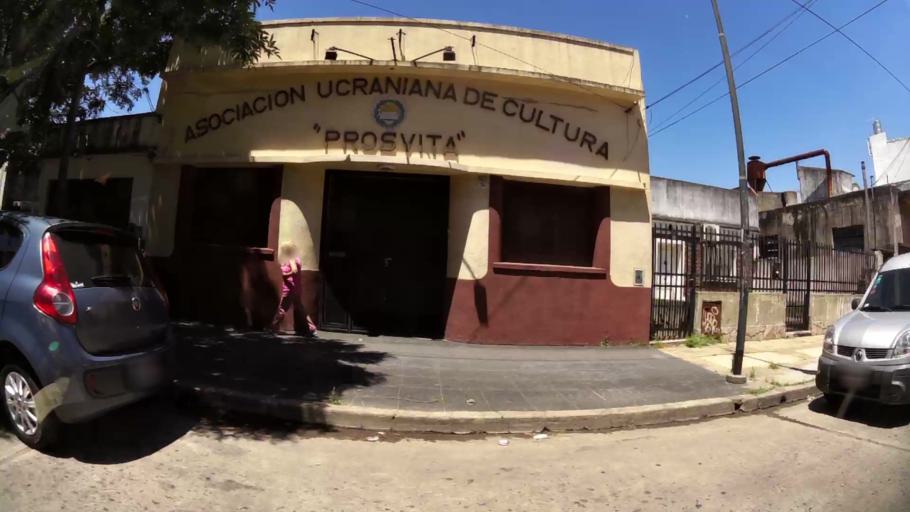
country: AR
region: Buenos Aires
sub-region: Partido de General San Martin
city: General San Martin
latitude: -34.5834
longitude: -58.5441
